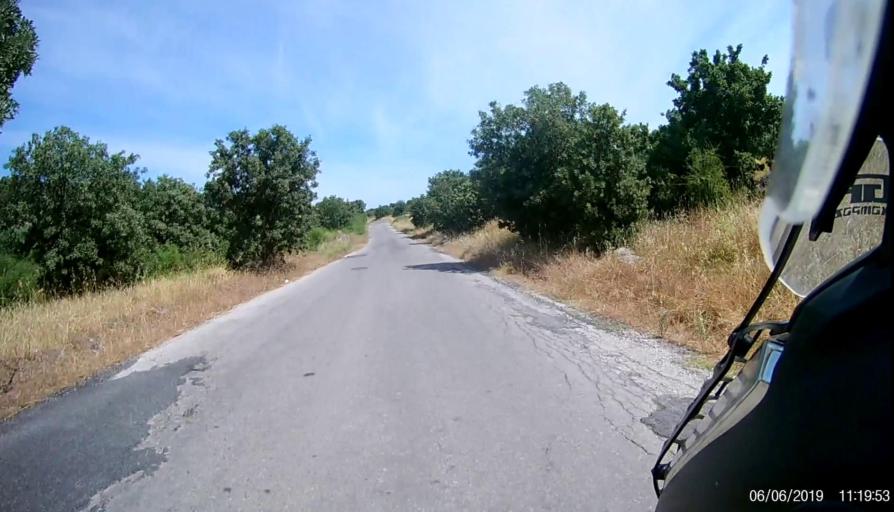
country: TR
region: Canakkale
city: Gulpinar
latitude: 39.6610
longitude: 26.1641
